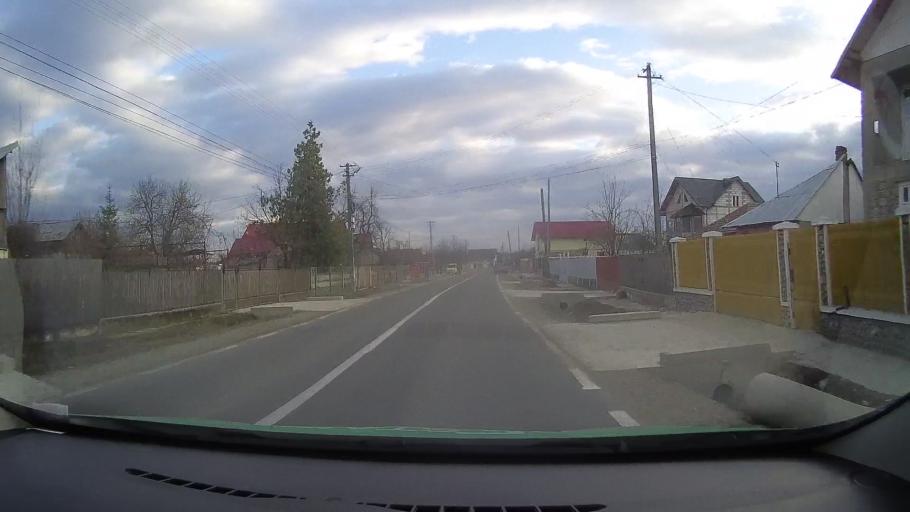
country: RO
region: Dambovita
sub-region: Comuna I. L. Caragiale
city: Mija
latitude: 44.9254
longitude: 25.6907
